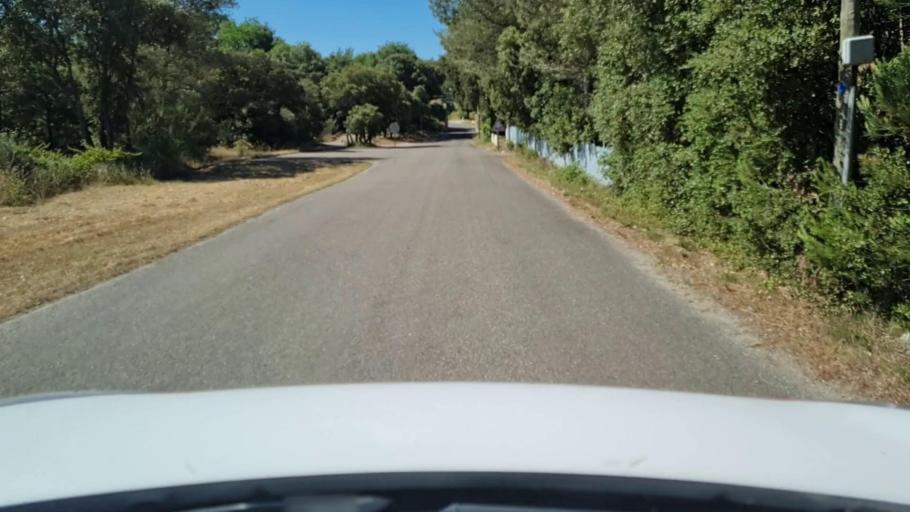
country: FR
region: Languedoc-Roussillon
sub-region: Departement du Gard
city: Villevieille
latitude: 43.7784
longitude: 4.1193
